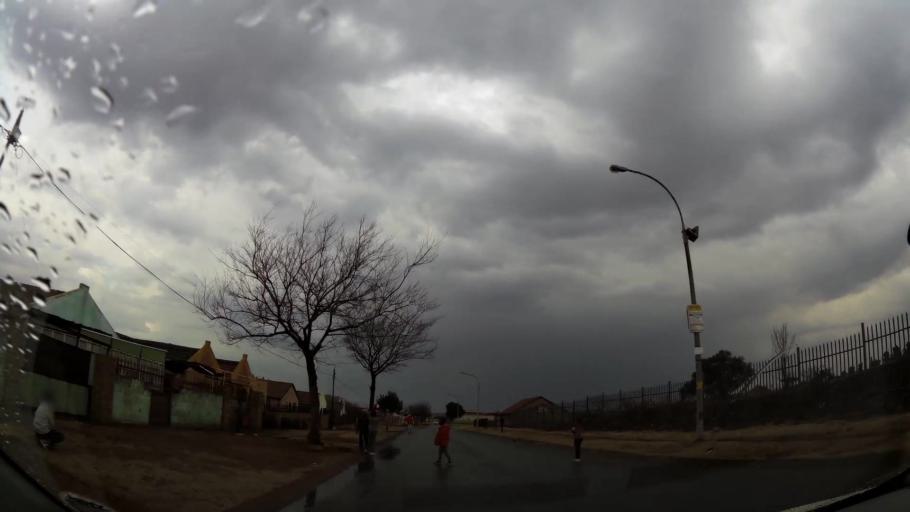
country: ZA
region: Gauteng
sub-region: Ekurhuleni Metropolitan Municipality
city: Germiston
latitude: -26.3742
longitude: 28.1309
